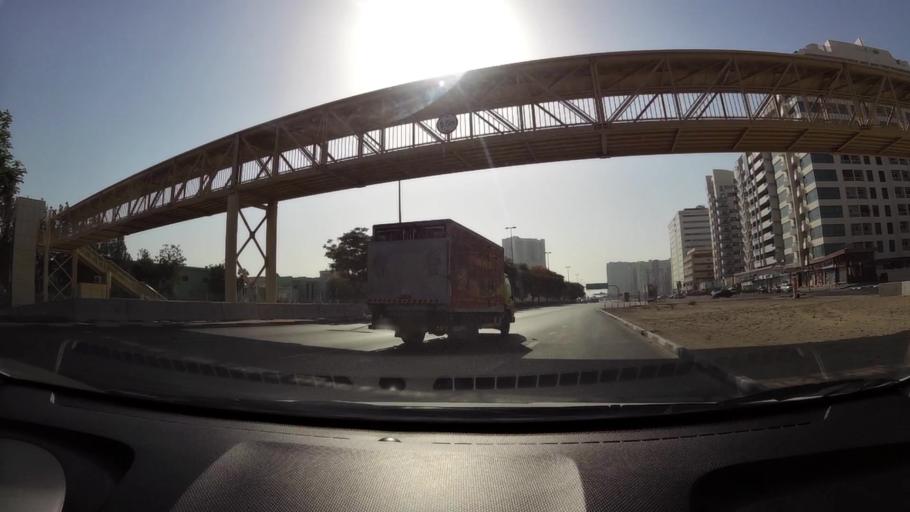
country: AE
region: Ash Shariqah
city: Sharjah
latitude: 25.2857
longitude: 55.3711
